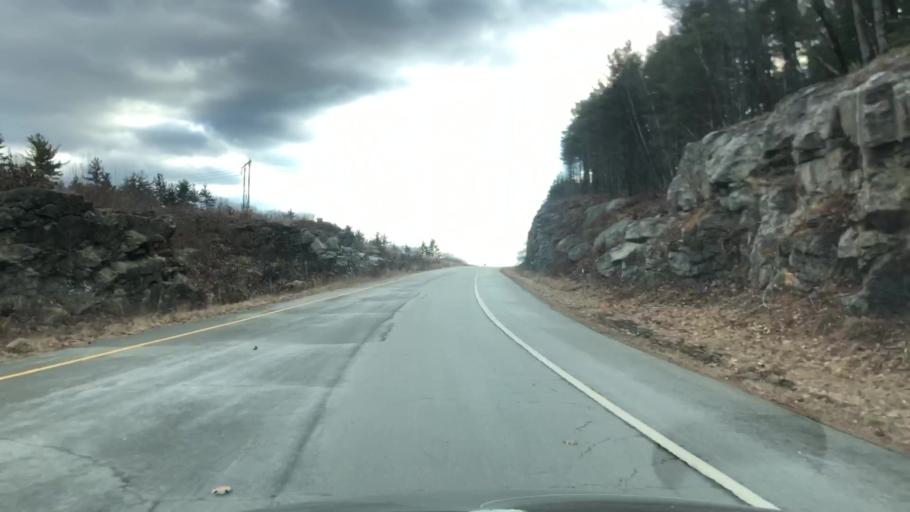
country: US
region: New Hampshire
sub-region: Hillsborough County
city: Milford
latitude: 42.8453
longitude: -71.6160
